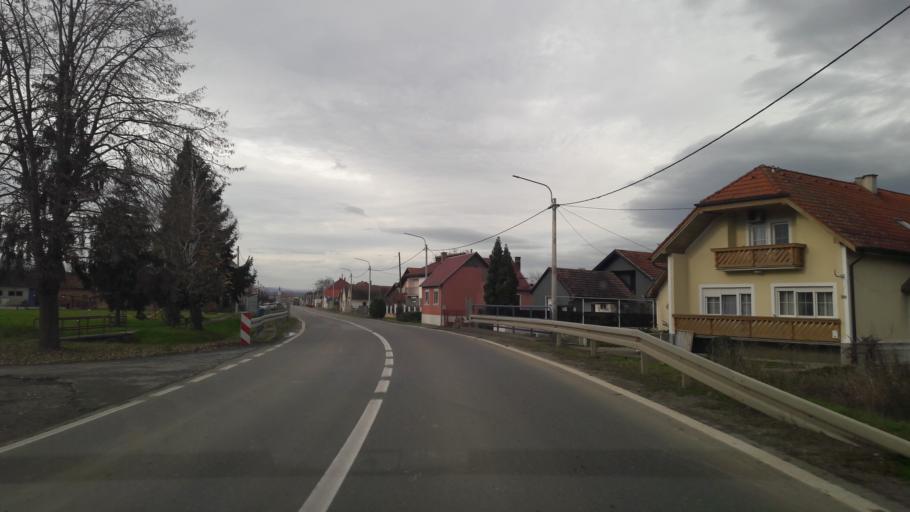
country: HR
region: Osjecko-Baranjska
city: Fericanci
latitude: 45.5234
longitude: 17.9951
